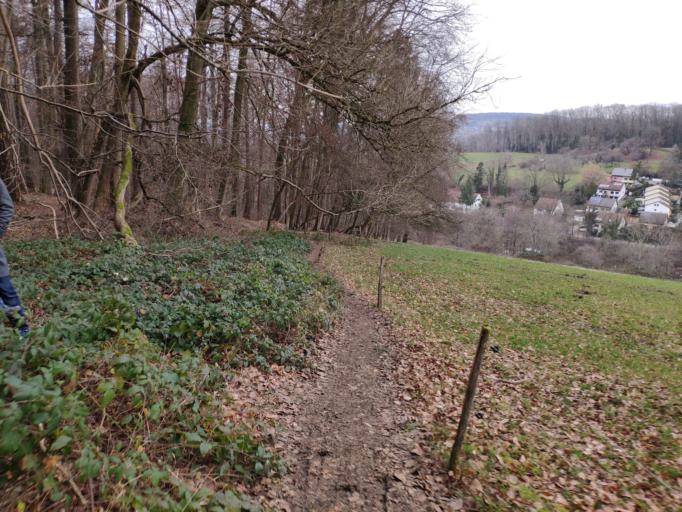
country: DE
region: Baden-Wuerttemberg
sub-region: Freiburg Region
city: Inzlingen
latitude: 47.5840
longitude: 7.6761
